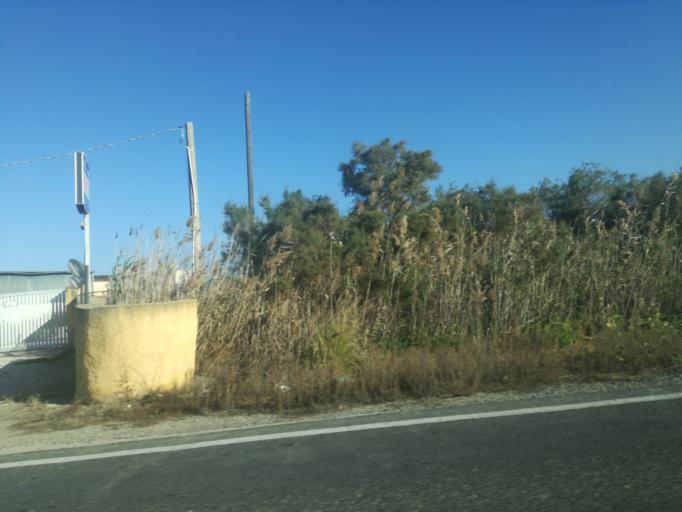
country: IT
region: Sicily
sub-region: Provincia di Caltanissetta
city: Gela
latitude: 37.0552
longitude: 14.2988
